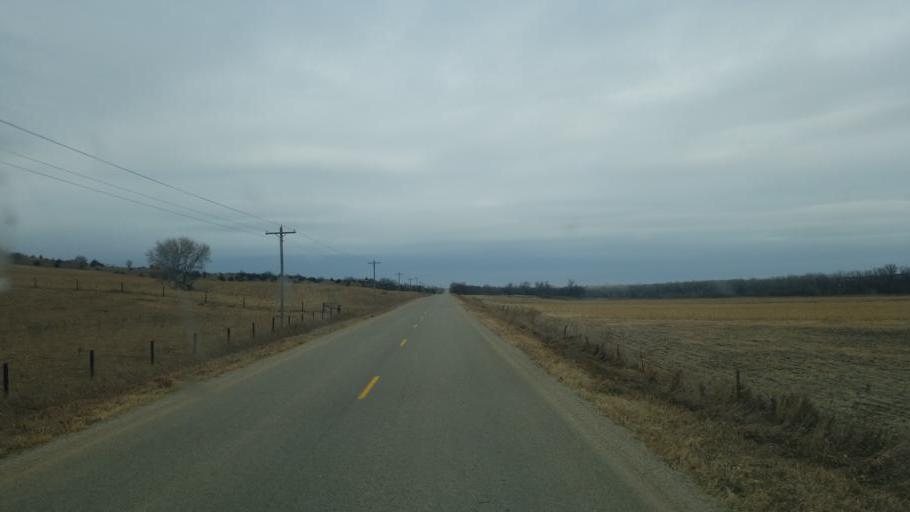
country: US
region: Nebraska
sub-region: Knox County
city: Center
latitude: 42.6469
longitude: -97.8872
